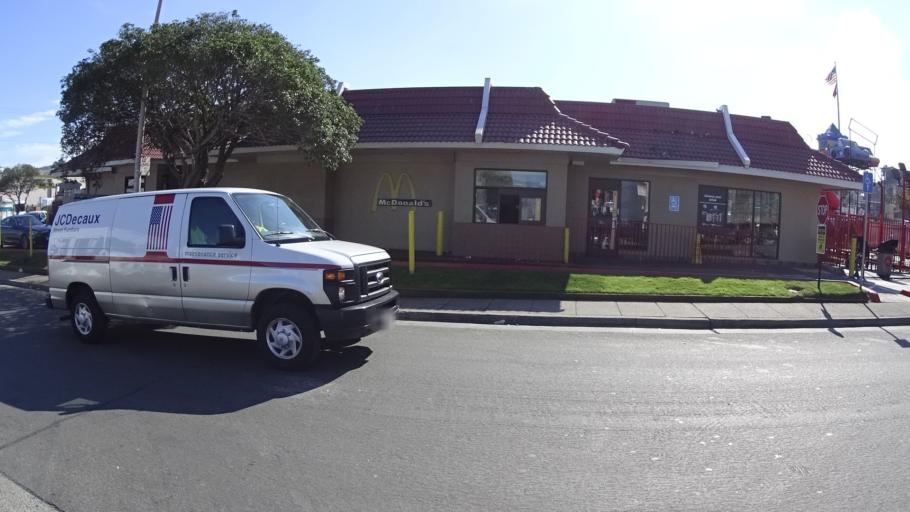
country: US
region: California
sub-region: San Francisco County
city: San Francisco
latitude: 37.7424
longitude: -122.4052
